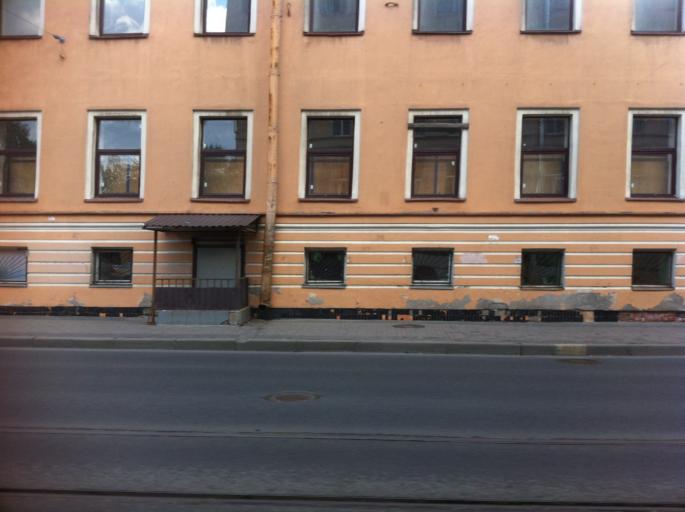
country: RU
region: St.-Petersburg
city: Admiralteisky
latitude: 59.9137
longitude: 30.2779
